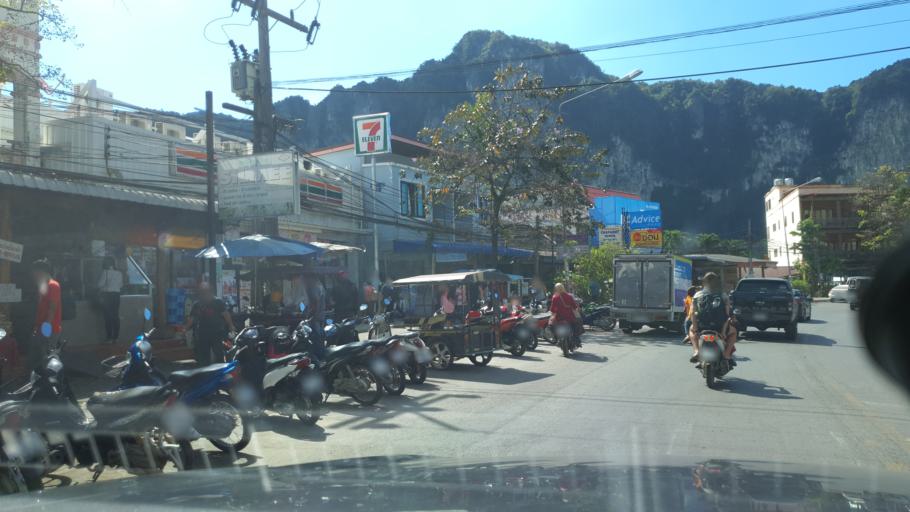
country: TH
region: Phangnga
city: Ban Ao Nang
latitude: 8.0365
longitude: 98.8336
